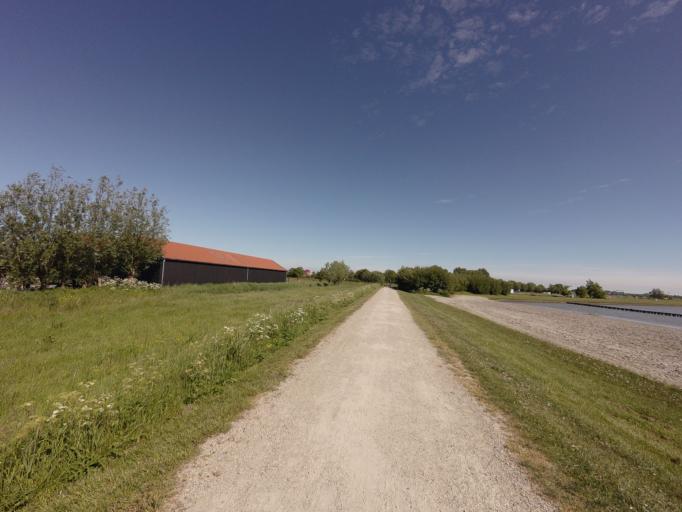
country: NL
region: North Holland
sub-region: Gemeente Uitgeest
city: Uitgeest
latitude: 52.5286
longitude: 4.7318
